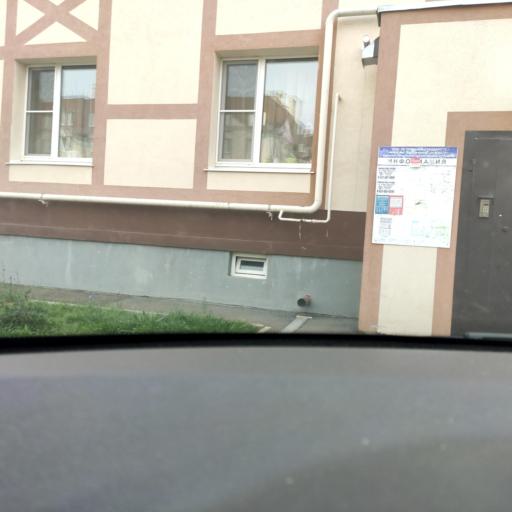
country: RU
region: Samara
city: Petra-Dubrava
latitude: 53.3075
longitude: 50.3158
